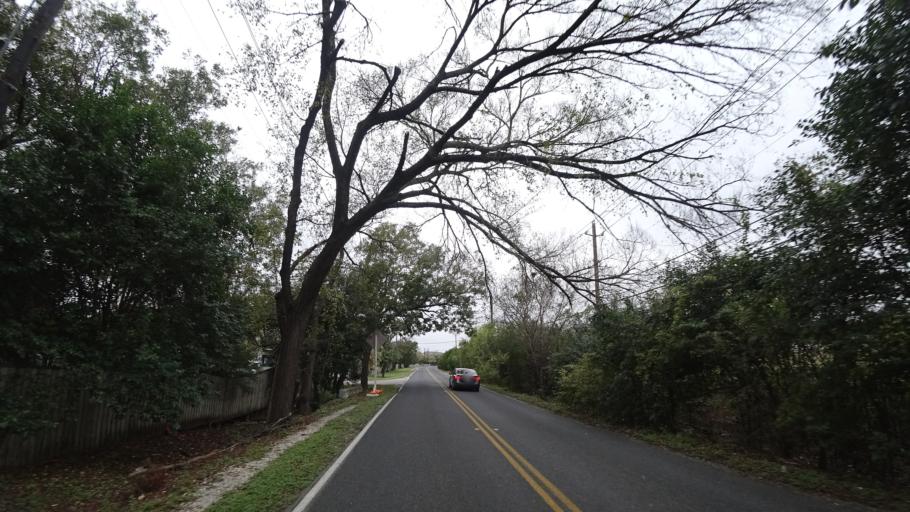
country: US
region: Texas
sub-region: Travis County
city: Barton Creek
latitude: 30.2479
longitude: -97.8844
